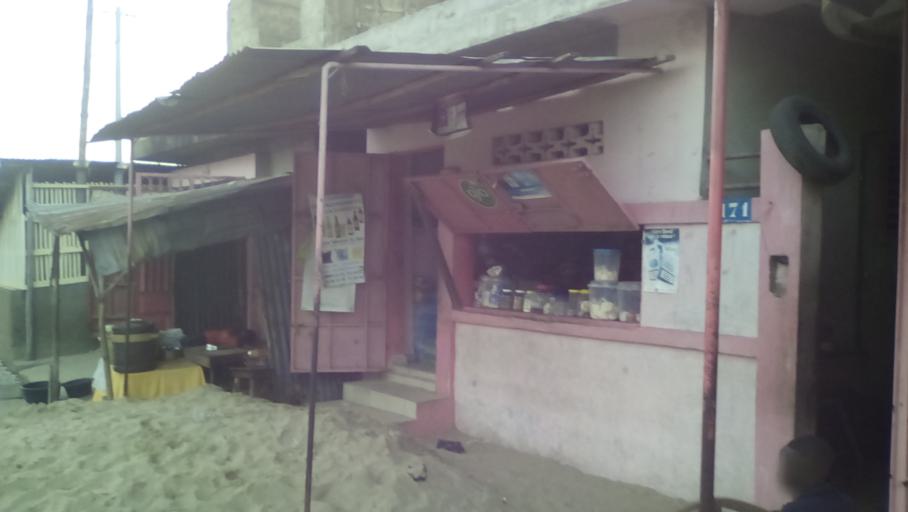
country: BJ
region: Littoral
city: Cotonou
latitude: 6.3812
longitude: 2.4405
